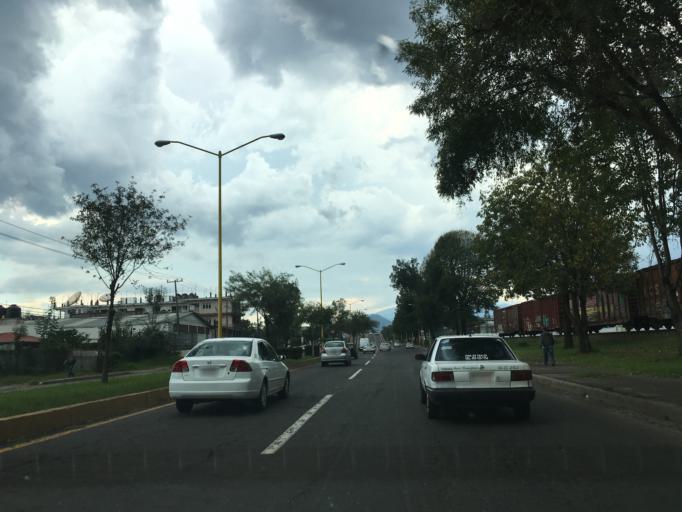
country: MX
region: Michoacan
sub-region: Uruapan
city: Toreo Bajo (El Toreo Bajo)
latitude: 19.4238
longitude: -102.0206
